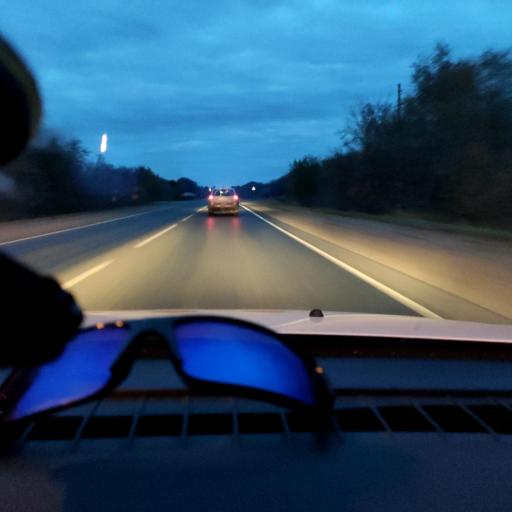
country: RU
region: Samara
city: Samara
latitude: 53.0808
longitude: 50.0972
